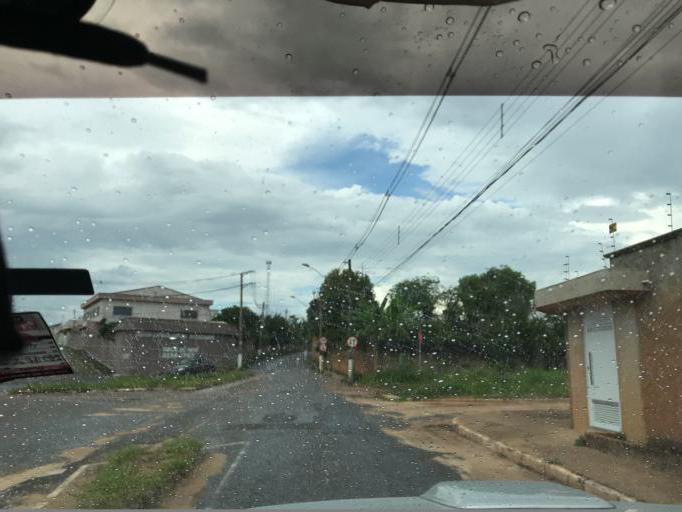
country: BR
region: Minas Gerais
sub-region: Tres Coracoes
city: Tres Coracoes
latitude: -21.7071
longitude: -45.2532
